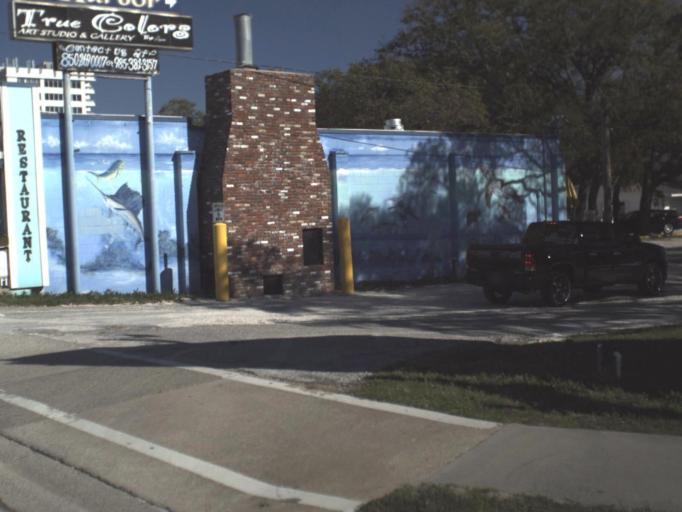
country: US
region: Florida
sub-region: Okaloosa County
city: Destin
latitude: 30.3941
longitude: -86.5052
